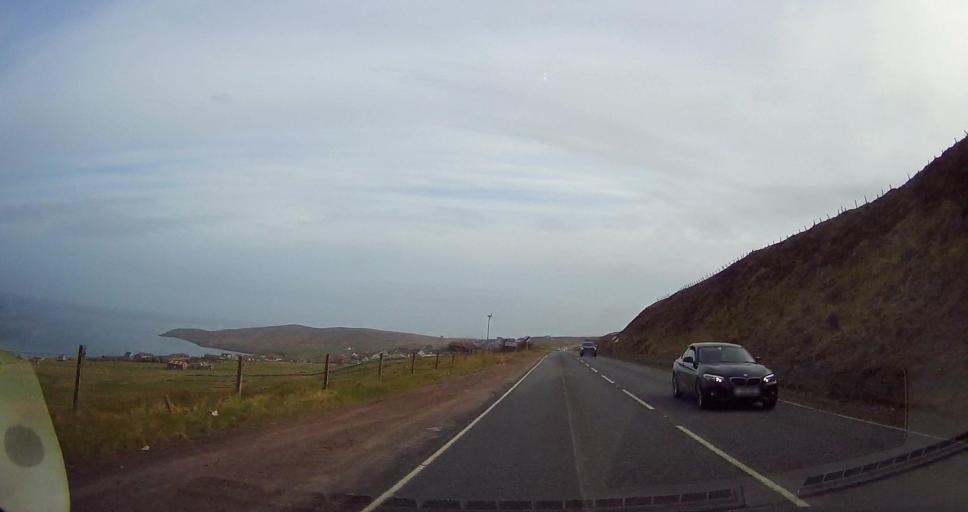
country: GB
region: Scotland
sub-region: Shetland Islands
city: Lerwick
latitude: 60.1358
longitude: -1.2141
